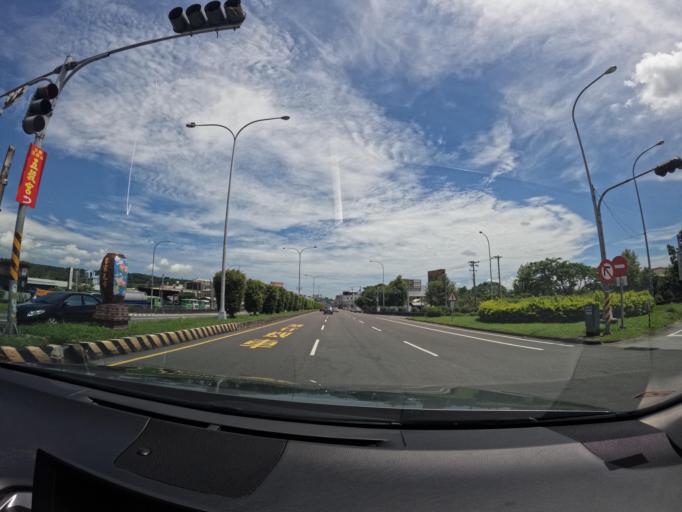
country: TW
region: Taiwan
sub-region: Miaoli
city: Miaoli
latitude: 24.5248
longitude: 120.8202
